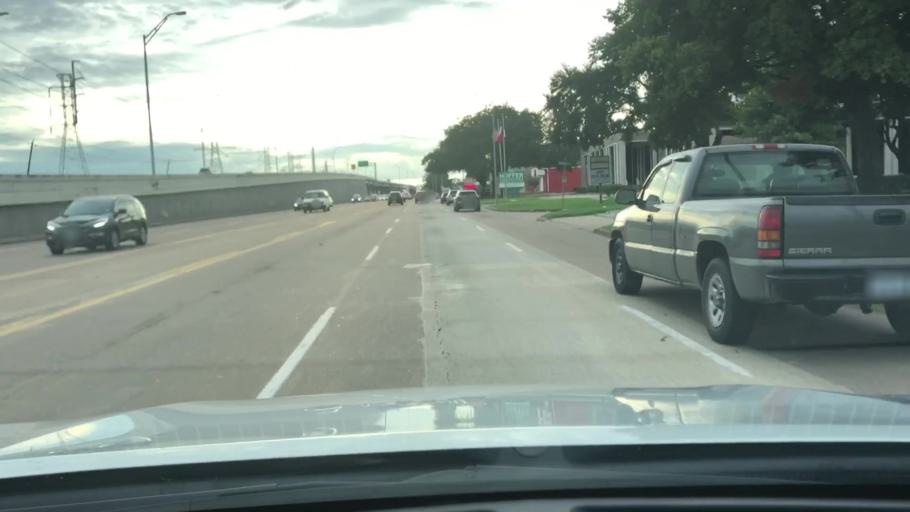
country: US
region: Texas
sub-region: Harris County
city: Piney Point Village
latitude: 29.7226
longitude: -95.5073
